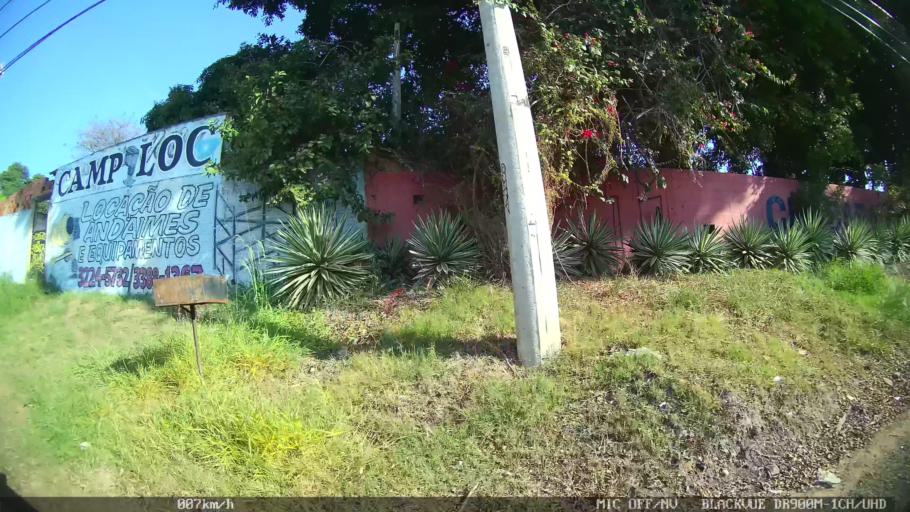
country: BR
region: Sao Paulo
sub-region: Campinas
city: Campinas
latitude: -22.9852
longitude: -47.1468
